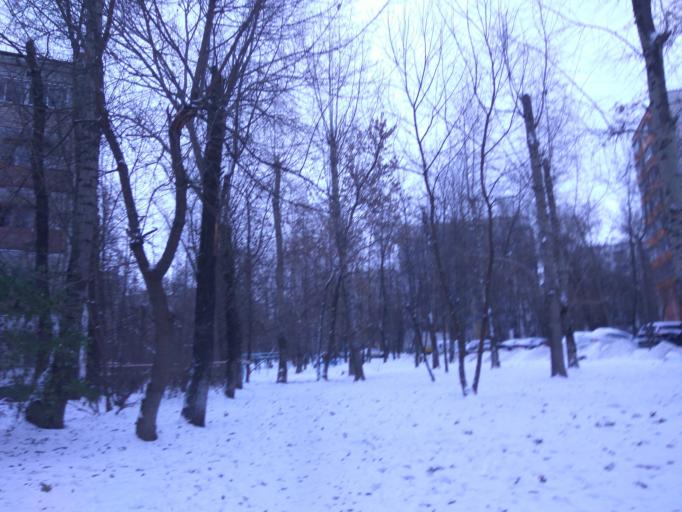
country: RU
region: Moscow
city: Tsaritsyno
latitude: 55.6353
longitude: 37.6498
